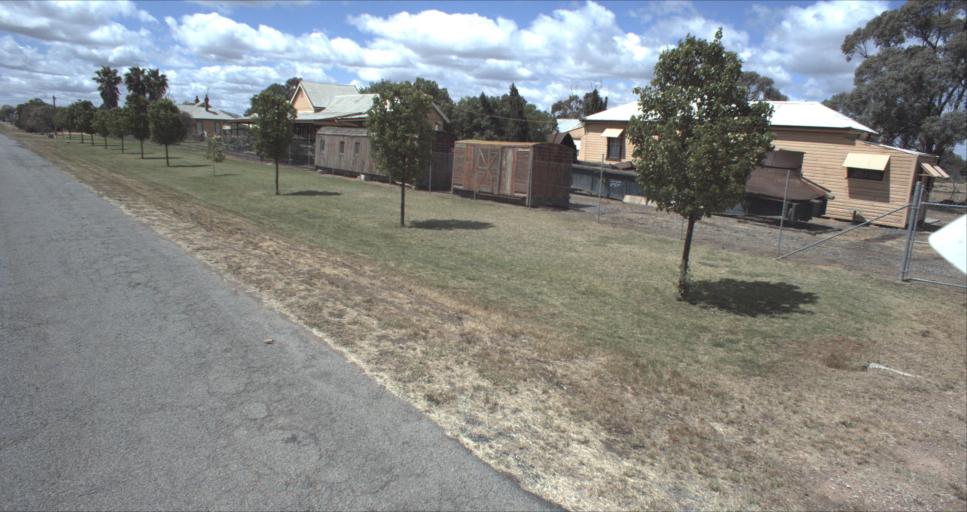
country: AU
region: New South Wales
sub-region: Murrumbidgee Shire
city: Darlington Point
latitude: -34.5196
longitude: 146.1804
